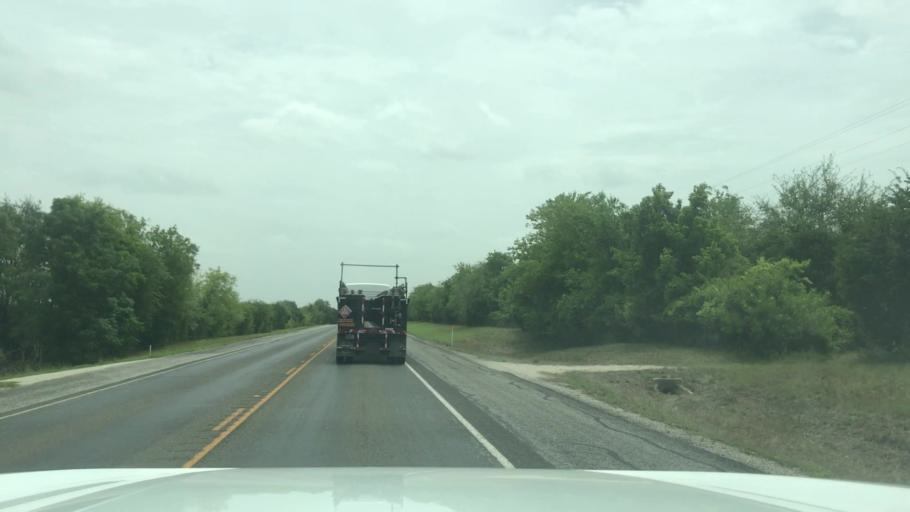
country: US
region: Texas
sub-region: Bosque County
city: Meridian
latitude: 31.8701
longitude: -97.6363
